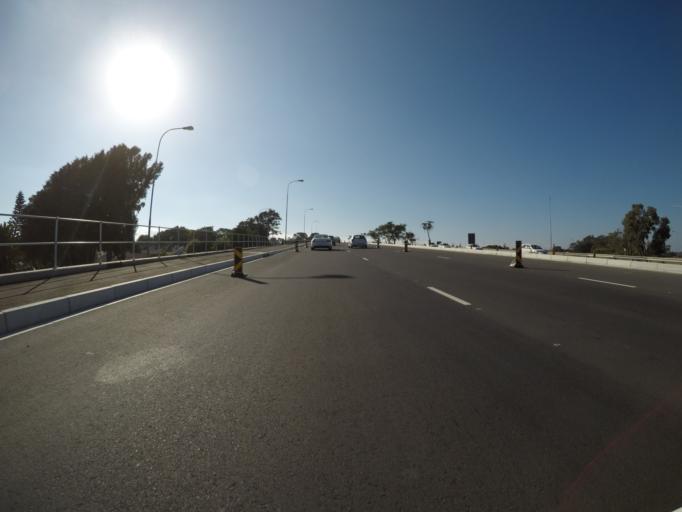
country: ZA
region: Western Cape
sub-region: City of Cape Town
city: Kraaifontein
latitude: -33.8785
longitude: 18.6603
